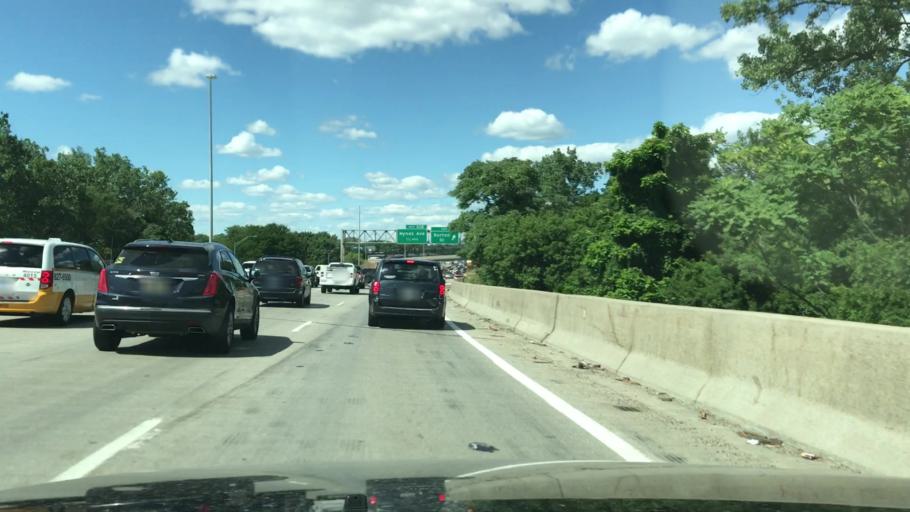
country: US
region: Michigan
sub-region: Kent County
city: Wyoming
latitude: 42.9249
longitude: -85.6820
